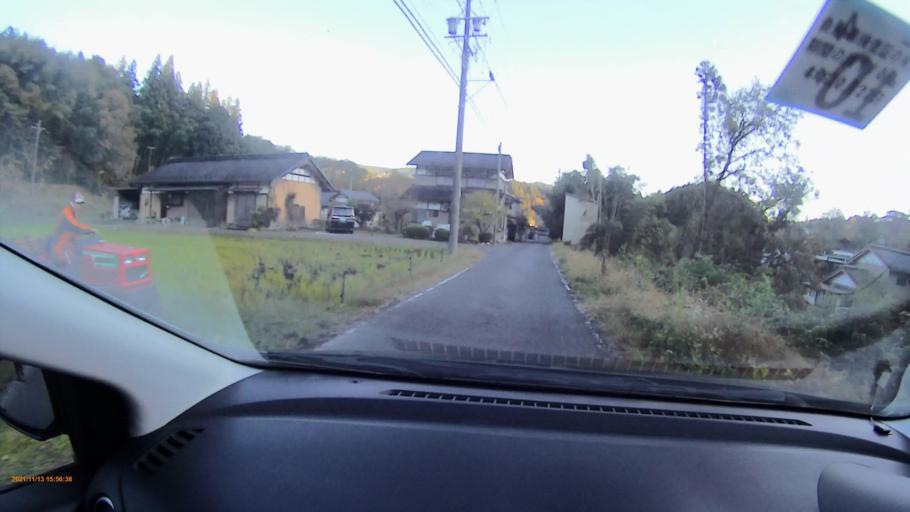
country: JP
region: Gifu
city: Nakatsugawa
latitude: 35.5928
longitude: 137.4563
